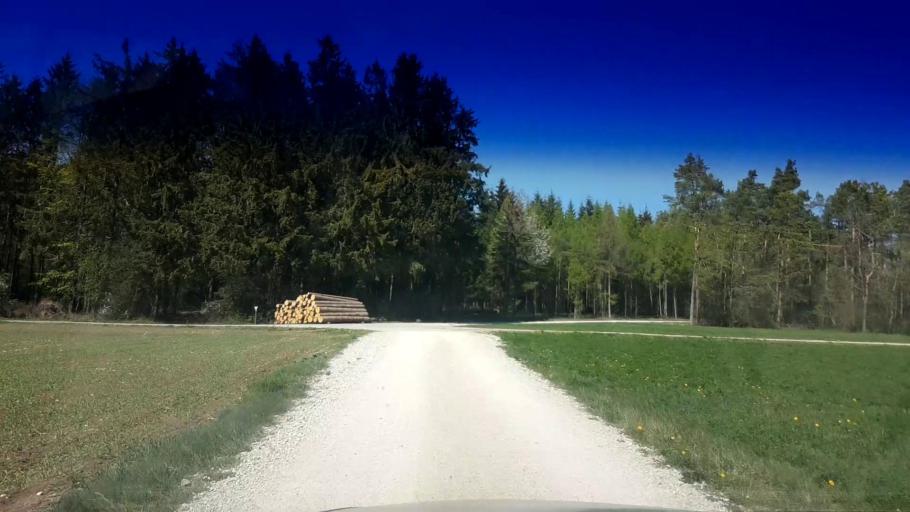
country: DE
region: Bavaria
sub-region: Upper Franconia
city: Poxdorf
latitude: 49.9334
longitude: 11.0870
